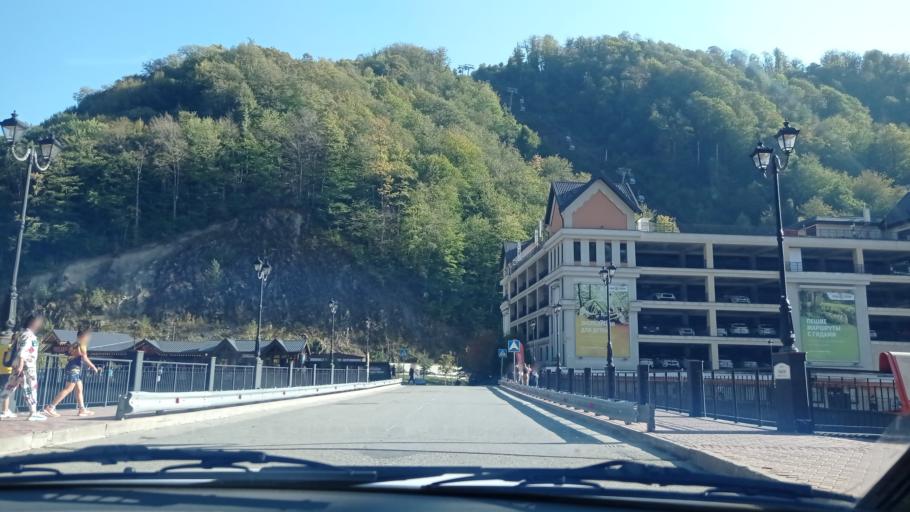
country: RU
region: Krasnodarskiy
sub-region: Sochi City
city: Krasnaya Polyana
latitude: 43.6732
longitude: 40.2984
